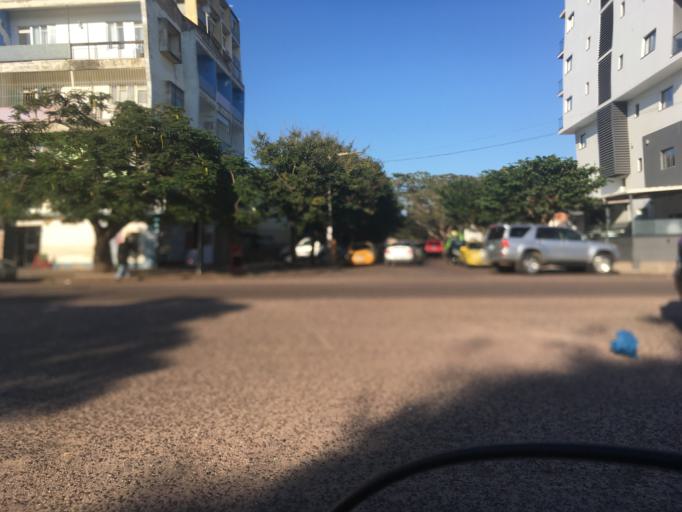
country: MZ
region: Maputo City
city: Maputo
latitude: -25.9647
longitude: 32.5917
